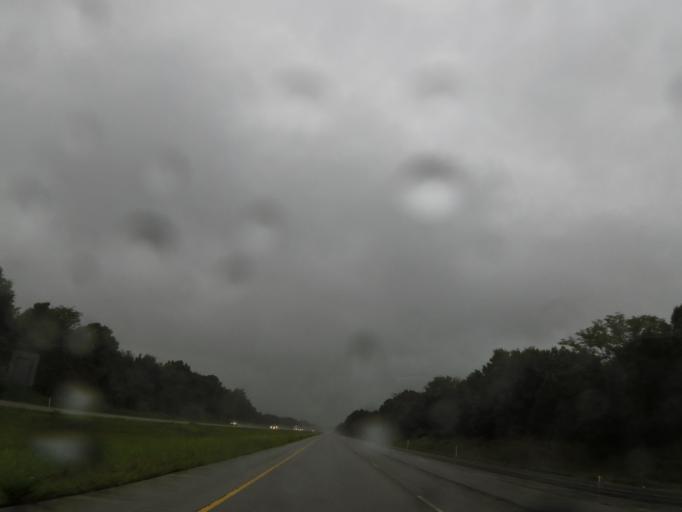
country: US
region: Illinois
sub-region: Johnson County
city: Vienna
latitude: 37.4507
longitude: -88.8877
